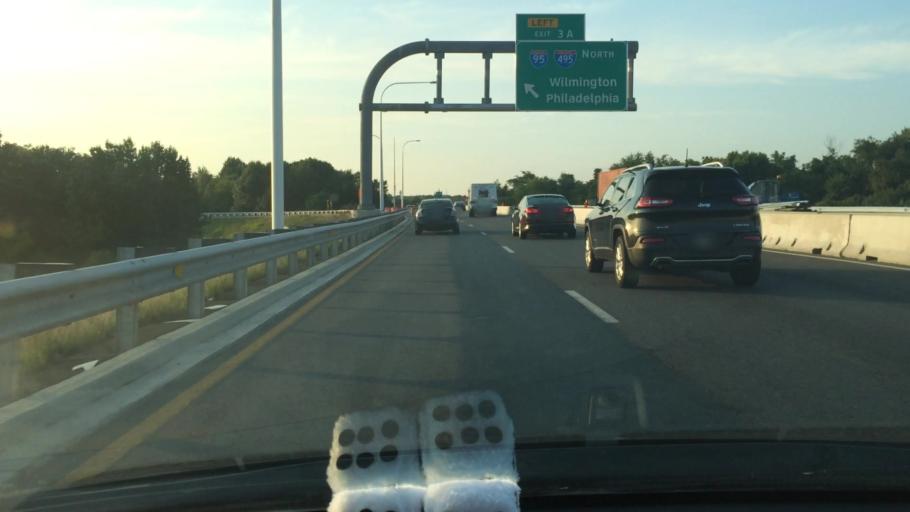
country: US
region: Delaware
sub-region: New Castle County
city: Newport
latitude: 39.7010
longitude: -75.6016
